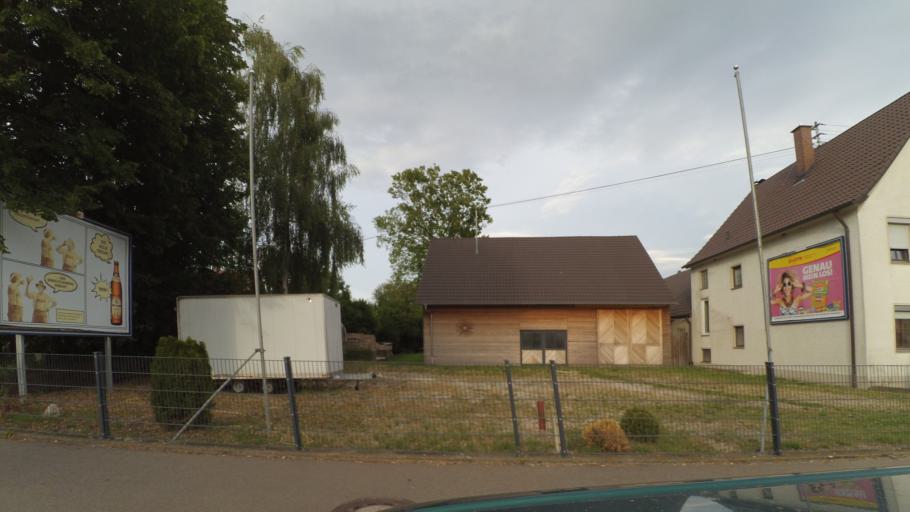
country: DE
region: Bavaria
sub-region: Swabia
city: Hochstadt an der Donau
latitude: 48.6153
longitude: 10.5670
